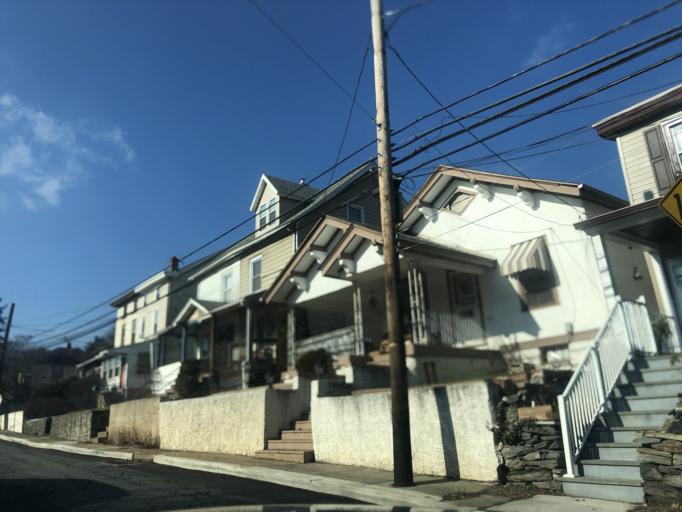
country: US
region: Pennsylvania
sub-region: Montgomery County
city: West Conshohocken
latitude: 40.0654
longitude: -75.3257
